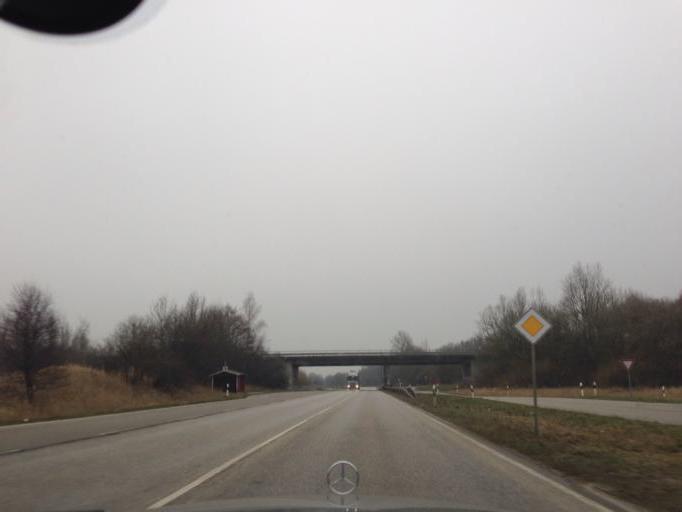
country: DE
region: Schleswig-Holstein
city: Kirchbarkau
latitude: 54.2249
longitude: 10.1463
